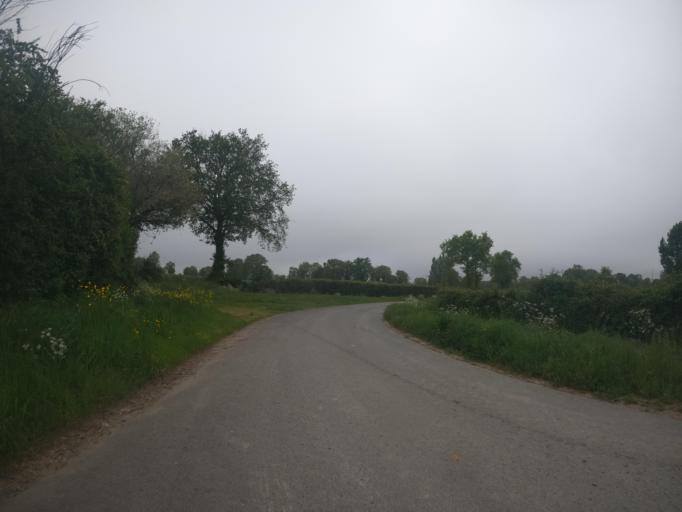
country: FR
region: Poitou-Charentes
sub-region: Departement des Deux-Sevres
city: Chiche
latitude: 46.8814
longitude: -0.3275
